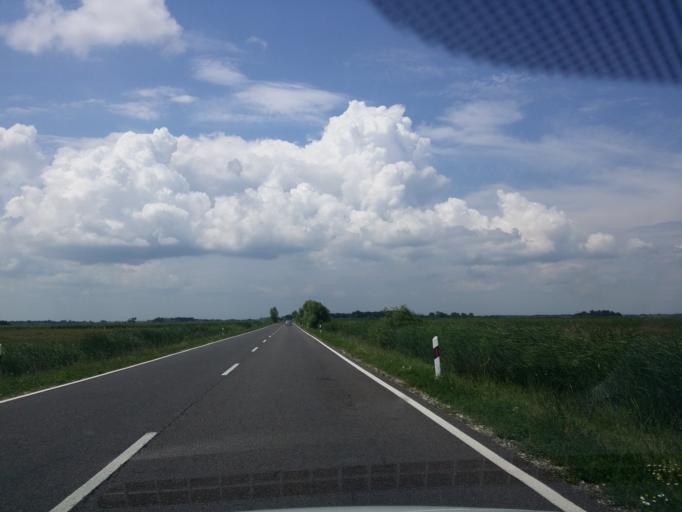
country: HU
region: Hajdu-Bihar
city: Egyek
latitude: 47.5543
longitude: 20.8745
